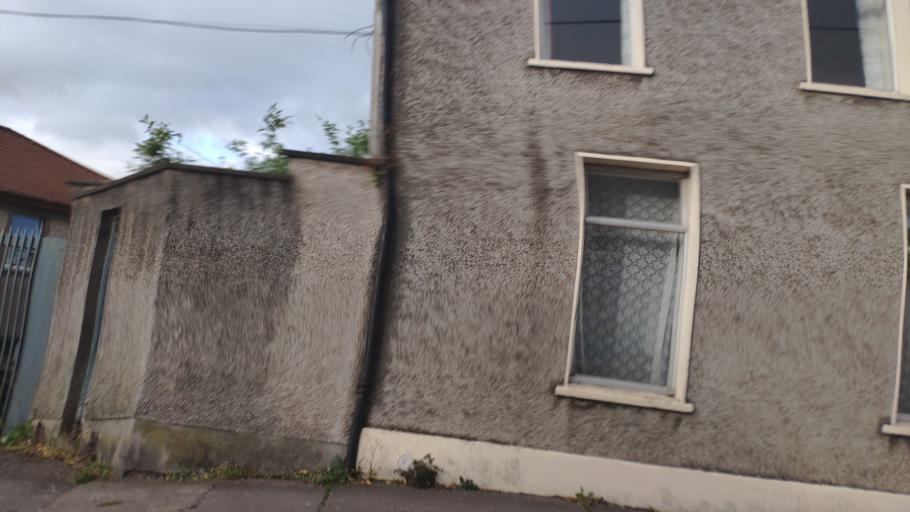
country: IE
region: Munster
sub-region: County Cork
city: Cork
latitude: 51.9061
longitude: -8.4807
